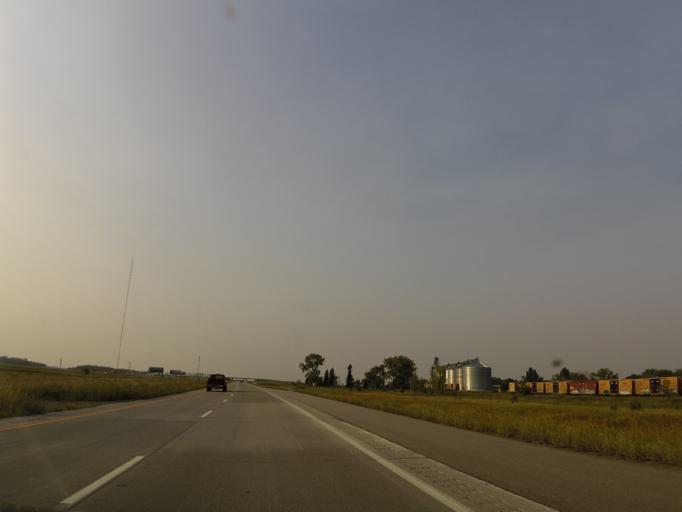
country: US
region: North Dakota
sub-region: Cass County
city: West Fargo
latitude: 47.1415
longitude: -96.9676
